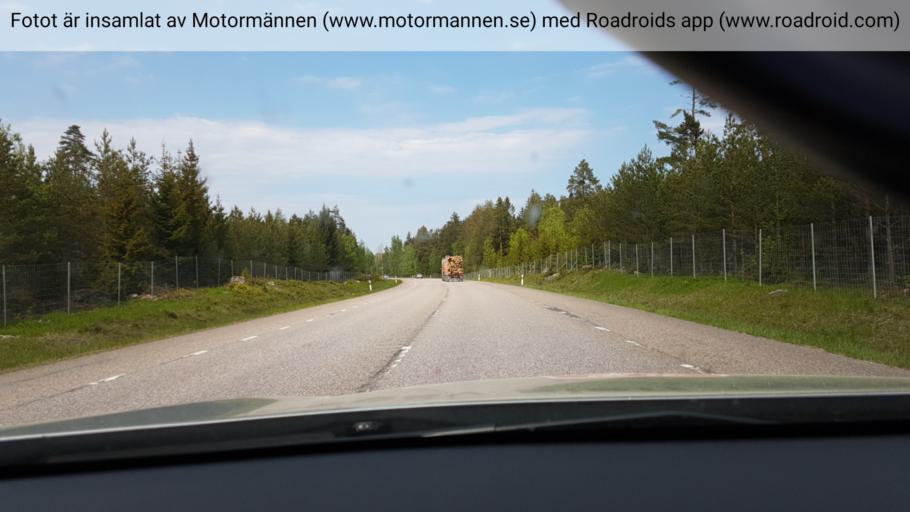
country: SE
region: Uppsala
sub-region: Alvkarleby Kommun
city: AElvkarleby
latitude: 60.5654
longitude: 17.4664
